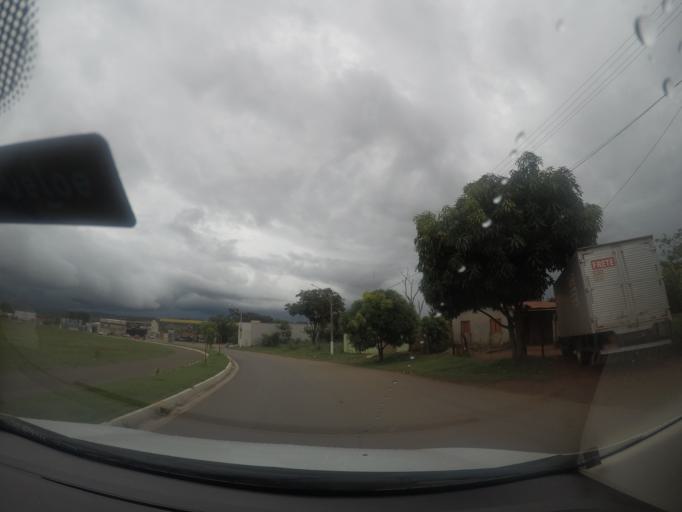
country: BR
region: Goias
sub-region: Trindade
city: Trindade
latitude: -16.6324
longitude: -49.3883
